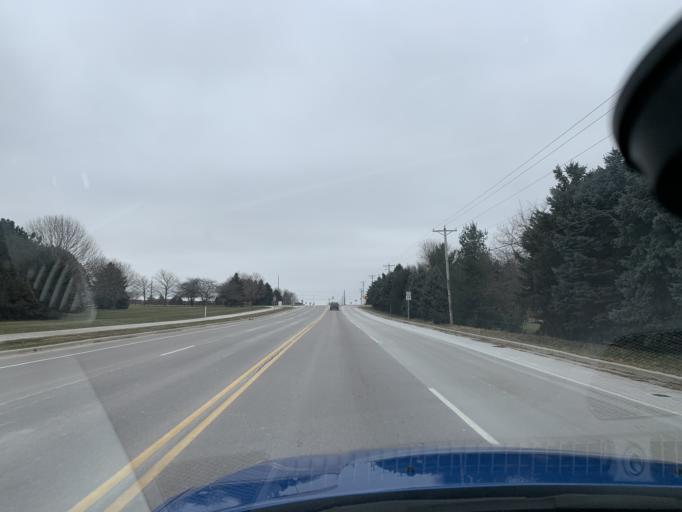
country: US
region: Wisconsin
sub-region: Dane County
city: Sun Prairie
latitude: 43.1906
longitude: -89.2644
